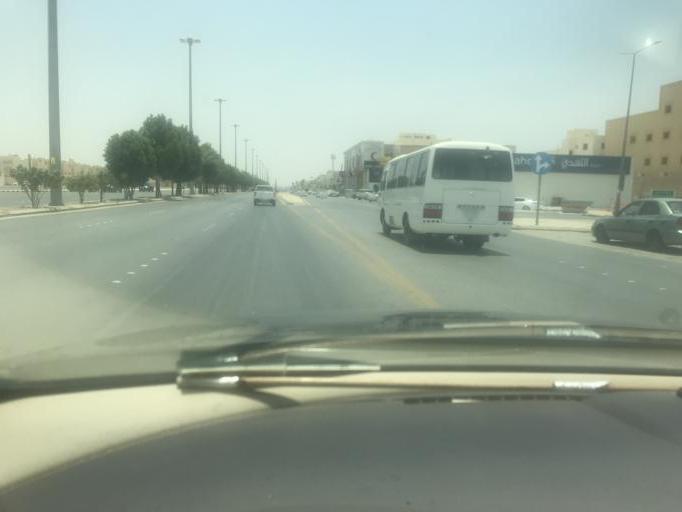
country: SA
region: Ar Riyad
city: Riyadh
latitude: 24.8227
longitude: 46.7503
